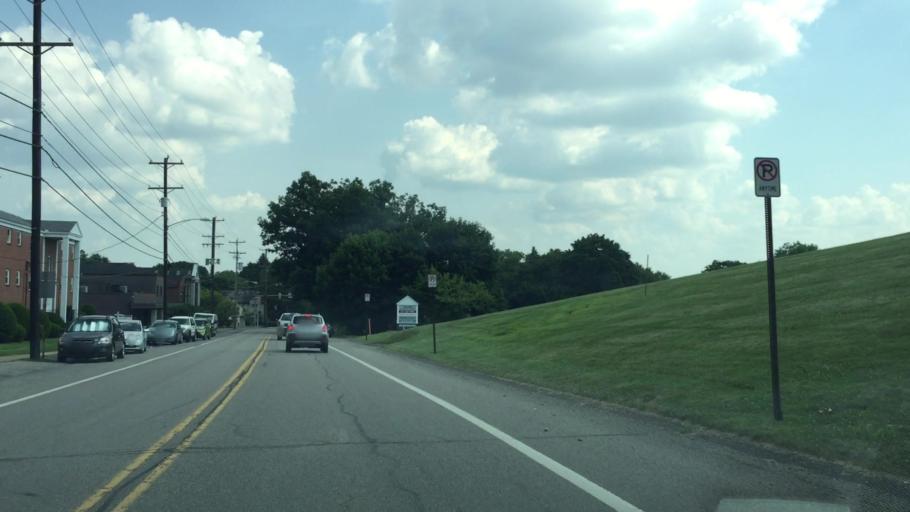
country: US
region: Pennsylvania
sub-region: Allegheny County
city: West View
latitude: 40.5314
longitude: -80.0357
